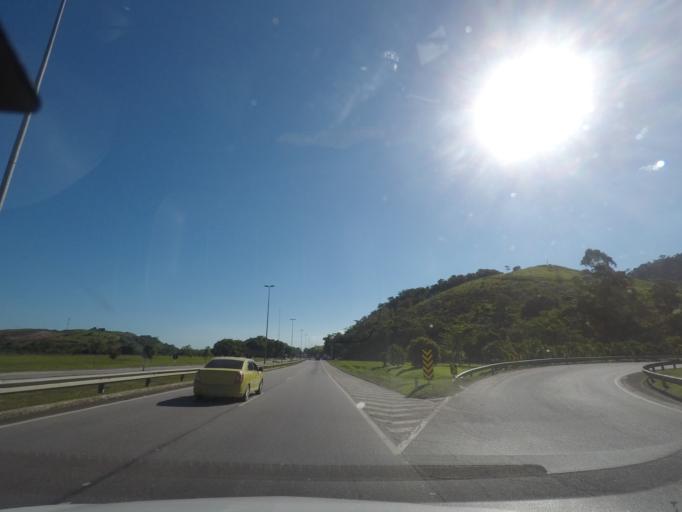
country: BR
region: Rio de Janeiro
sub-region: Guapimirim
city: Guapimirim
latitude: -22.6567
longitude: -43.0888
